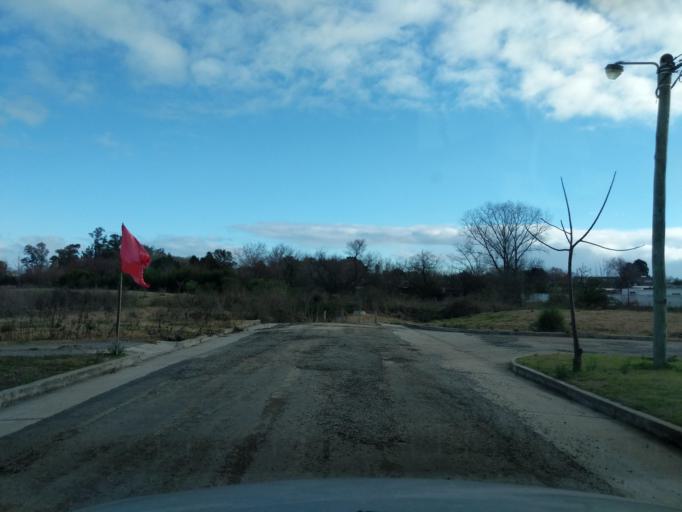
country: UY
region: Florida
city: Florida
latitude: -34.1018
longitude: -56.2228
